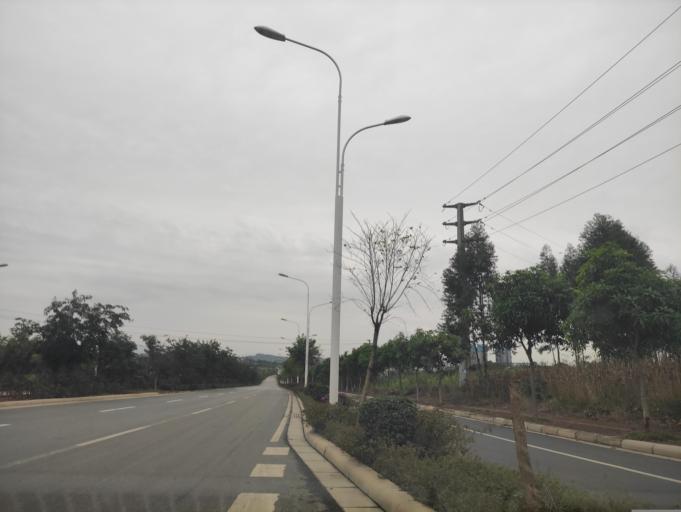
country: CN
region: Guangxi Zhuangzu Zizhiqu
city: Baise City
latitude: 23.7986
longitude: 106.7378
